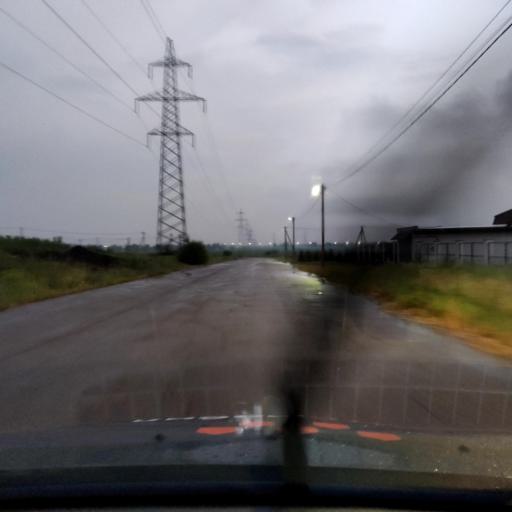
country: RU
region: Voronezj
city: Novaya Usman'
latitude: 51.6219
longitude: 39.3290
